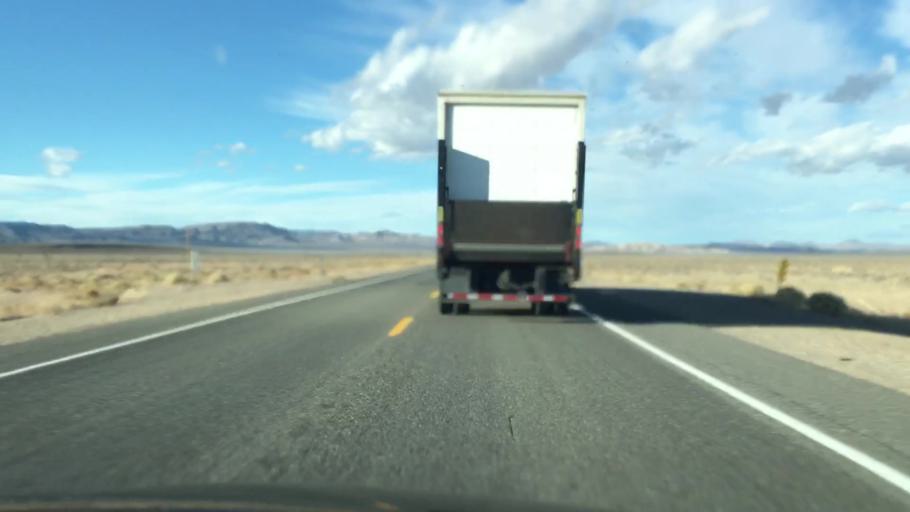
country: US
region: Nevada
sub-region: Esmeralda County
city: Goldfield
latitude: 37.4337
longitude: -117.1616
